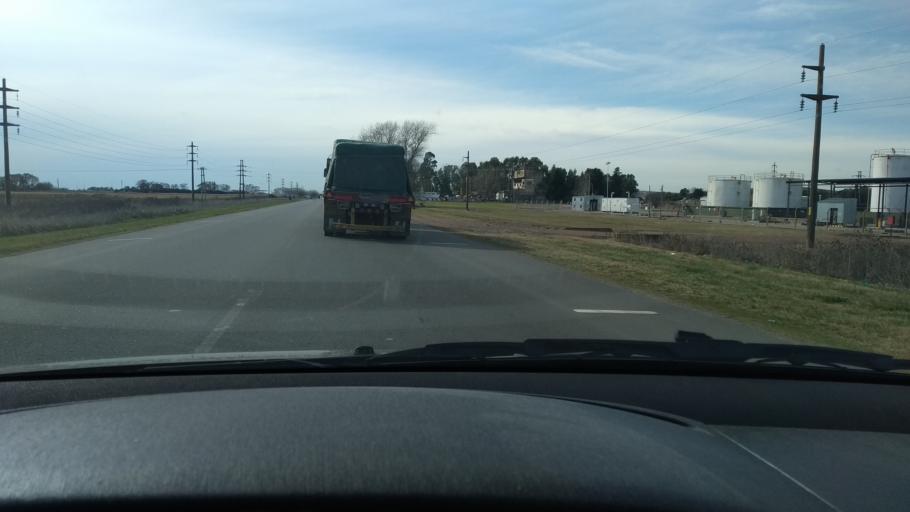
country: AR
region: Buenos Aires
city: Olavarria
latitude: -36.9422
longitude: -60.2370
